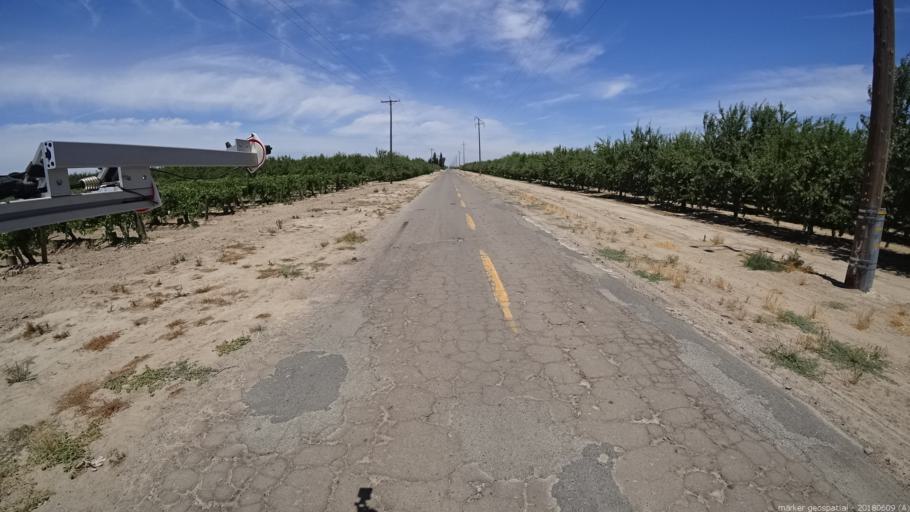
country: US
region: California
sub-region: Madera County
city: Parkwood
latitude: 36.8472
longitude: -120.1103
